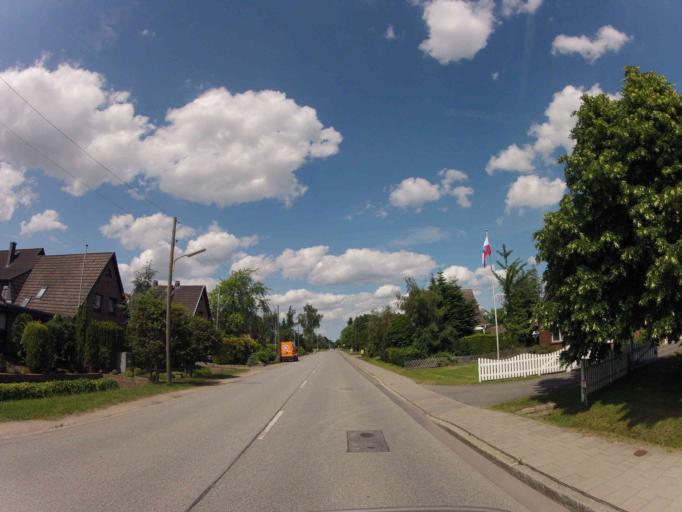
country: DE
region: Lower Saxony
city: Winsen
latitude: 53.4077
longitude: 10.1884
